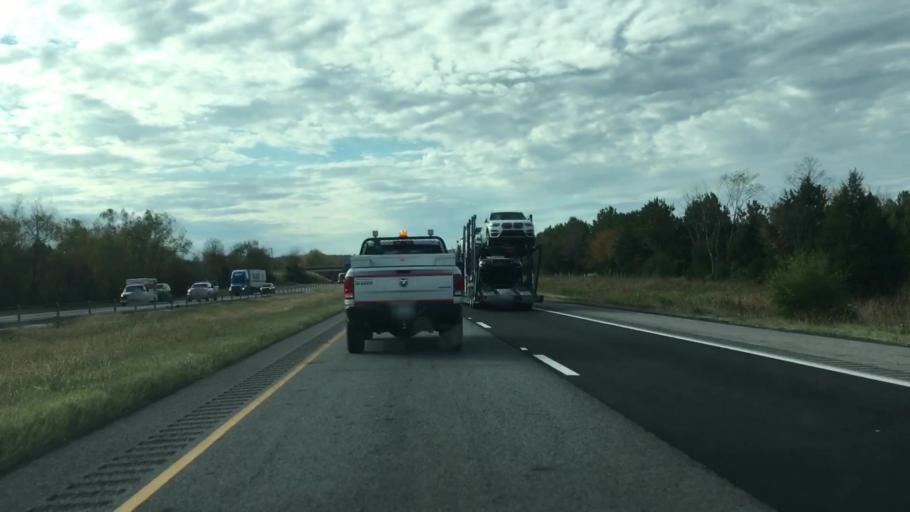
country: US
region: Arkansas
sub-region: Pope County
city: Atkins
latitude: 35.2503
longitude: -92.8858
